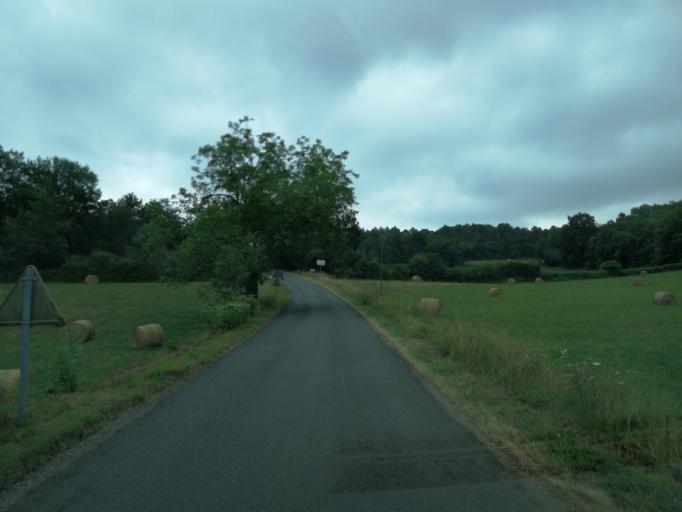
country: FR
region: Midi-Pyrenees
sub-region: Departement du Lot
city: Prayssac
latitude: 44.5387
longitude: 1.0816
